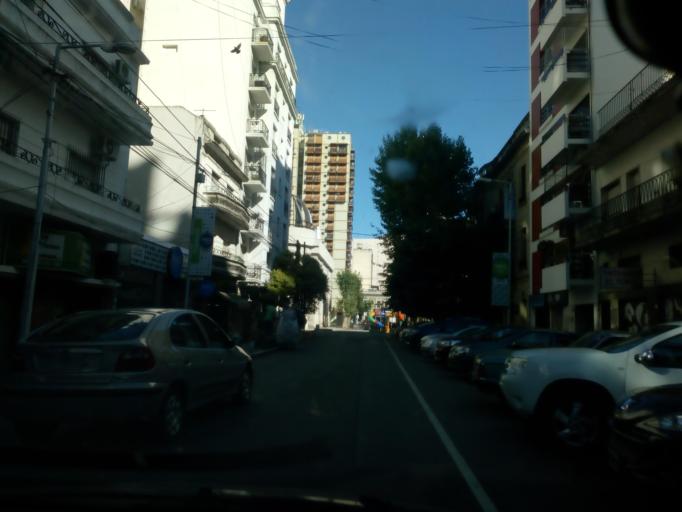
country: AR
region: Buenos Aires
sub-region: Partido de Avellaneda
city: Avellaneda
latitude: -34.6638
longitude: -58.3645
